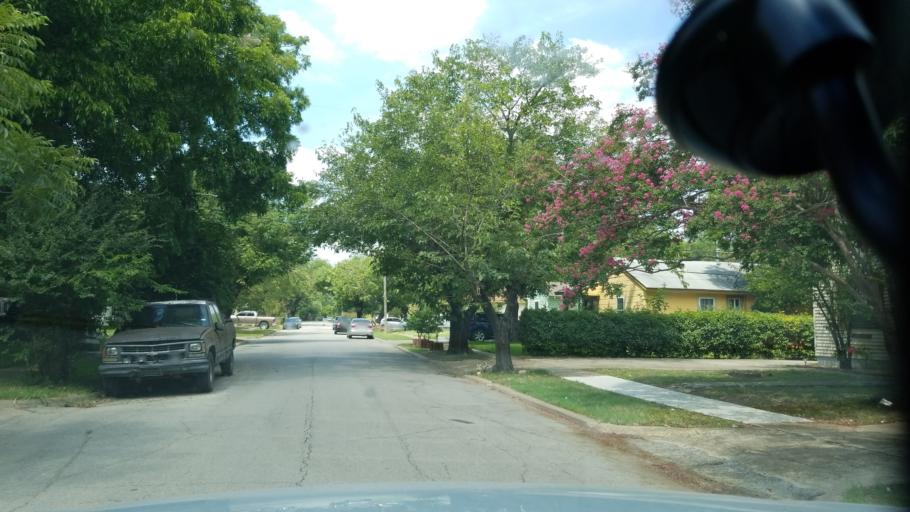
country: US
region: Texas
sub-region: Dallas County
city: Grand Prairie
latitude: 32.7558
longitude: -96.9782
